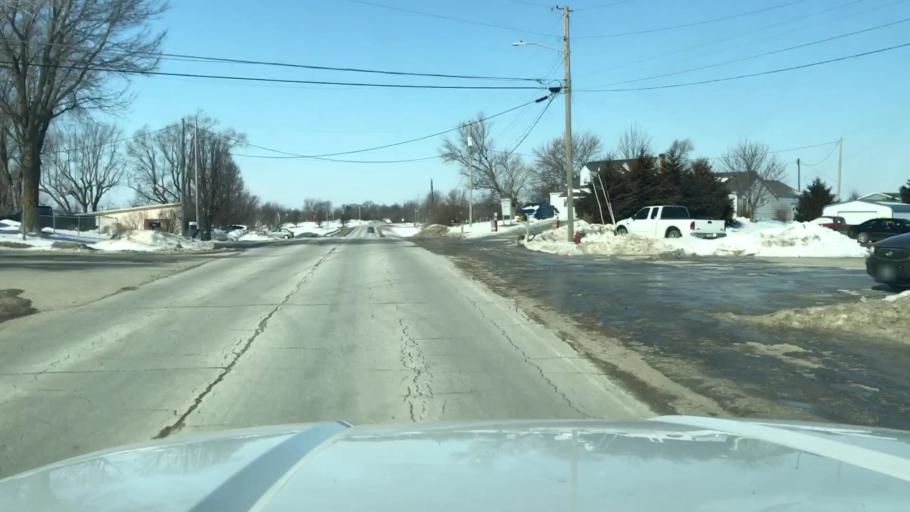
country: US
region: Missouri
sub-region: Andrew County
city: Savannah
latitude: 39.9483
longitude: -94.8411
